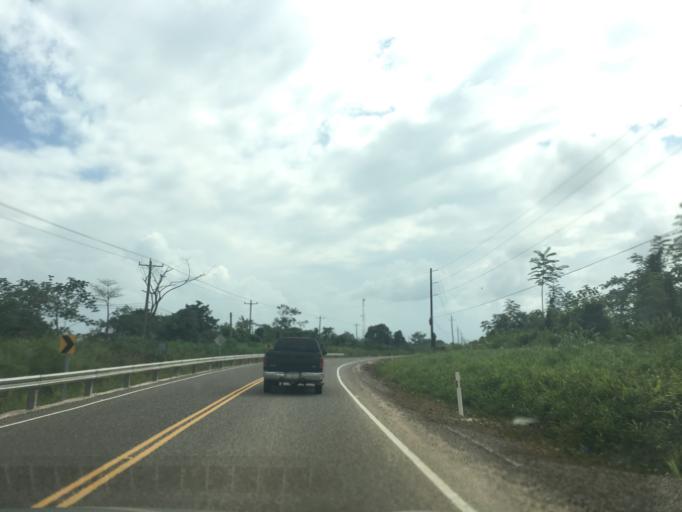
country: BZ
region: Stann Creek
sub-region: Dangriga
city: Dangriga
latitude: 16.9969
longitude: -88.3021
